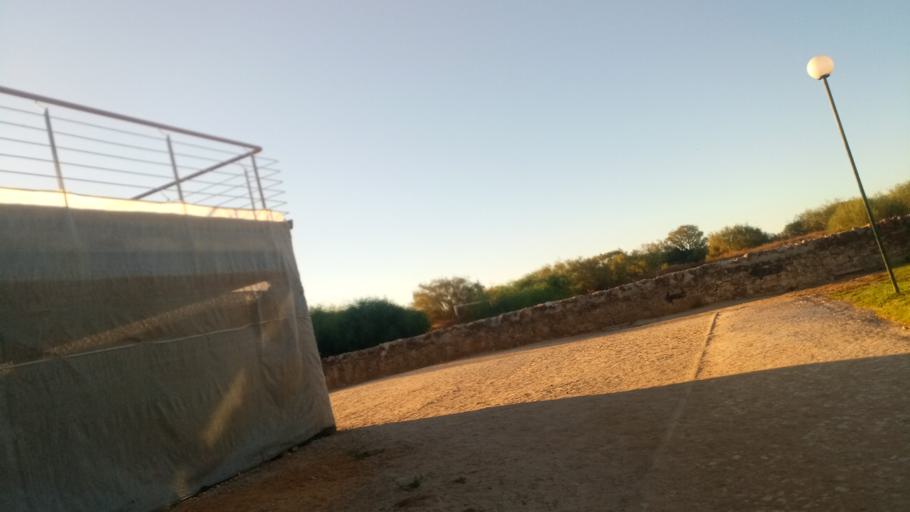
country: PT
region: Faro
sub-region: Tavira
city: Tavira
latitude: 37.1327
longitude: -7.6068
